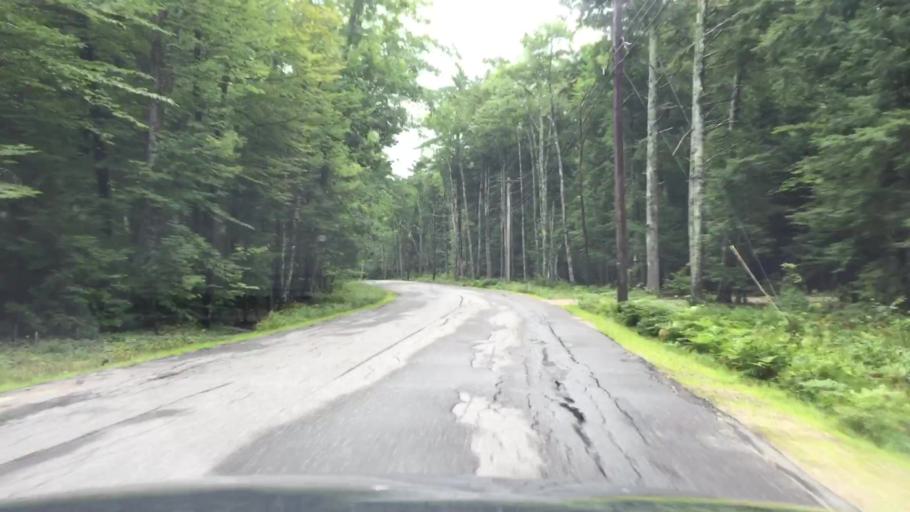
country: US
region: New Hampshire
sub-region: Carroll County
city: Center Harbor
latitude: 43.7275
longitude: -71.4843
